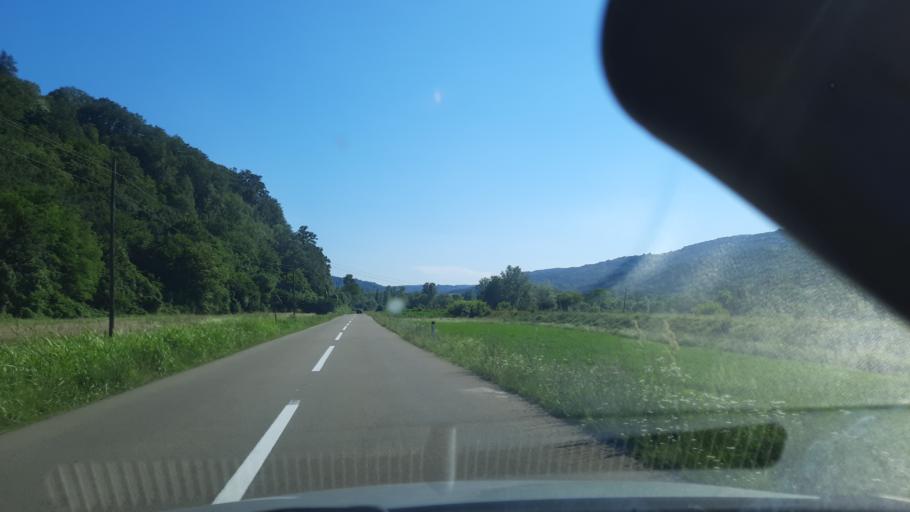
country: RS
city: Turija
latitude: 44.5111
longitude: 21.6352
